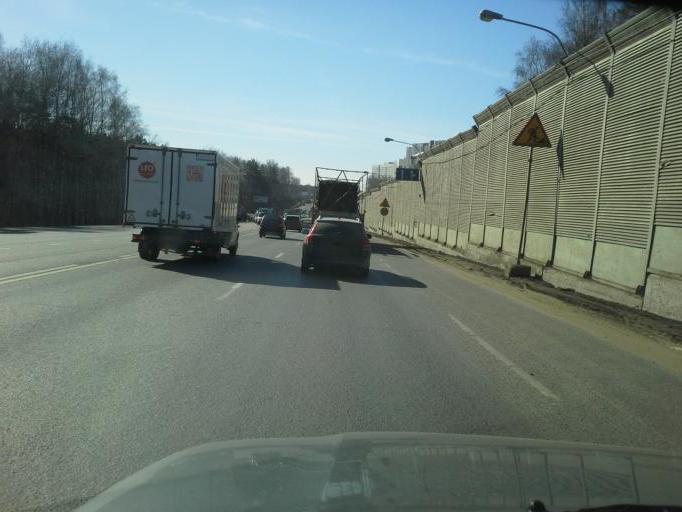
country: RU
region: Moskovskaya
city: Odintsovo
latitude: 55.6676
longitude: 37.3089
